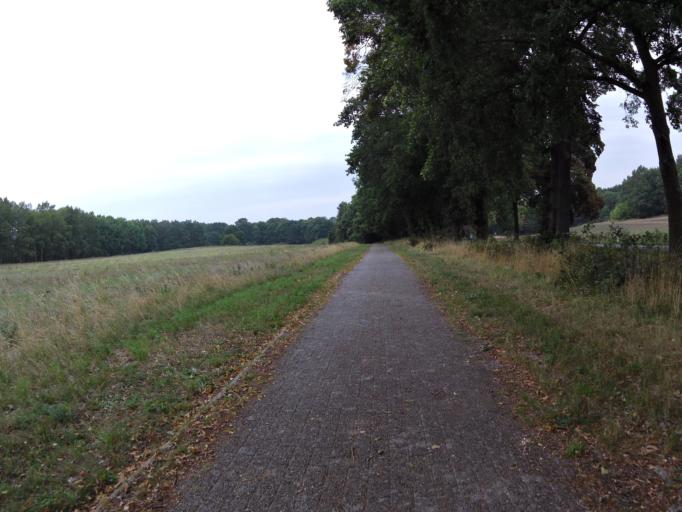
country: DE
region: Mecklenburg-Vorpommern
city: Seebad Heringsdorf
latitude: 53.8912
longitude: 14.1660
